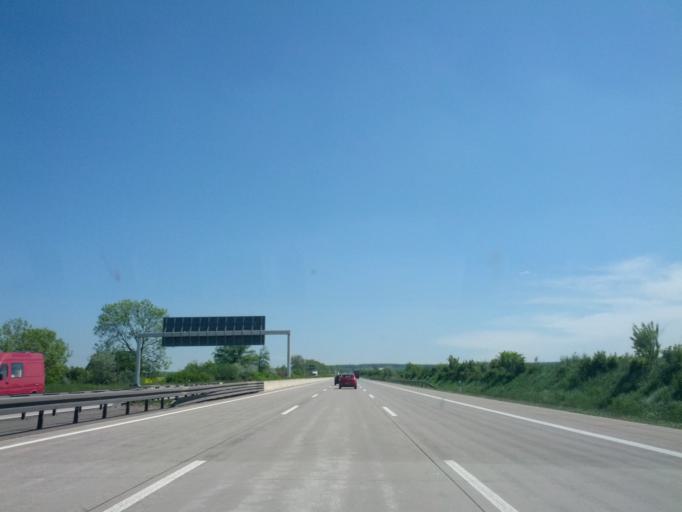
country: DE
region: Thuringia
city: Kirchheim
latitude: 50.9065
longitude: 11.0177
